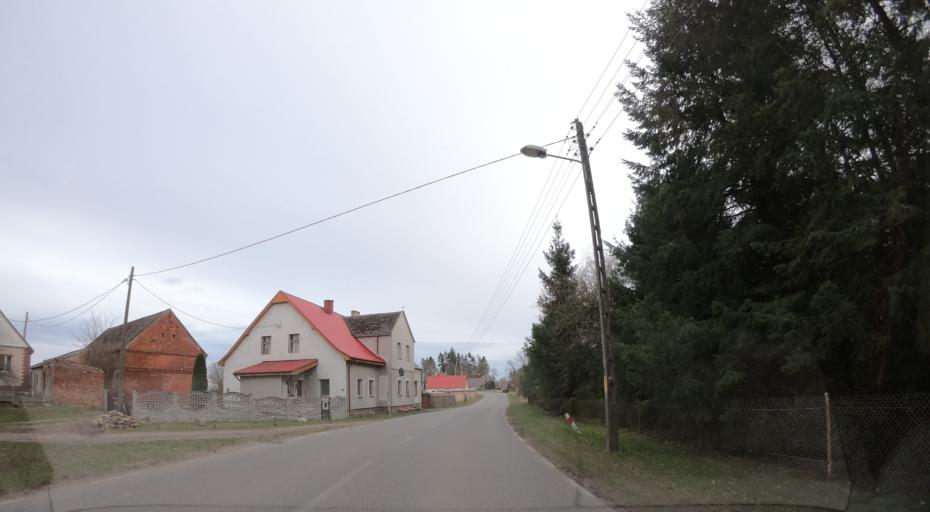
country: PL
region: West Pomeranian Voivodeship
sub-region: Powiat mysliborski
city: Nowogrodek Pomorski
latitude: 52.9079
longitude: 14.9604
